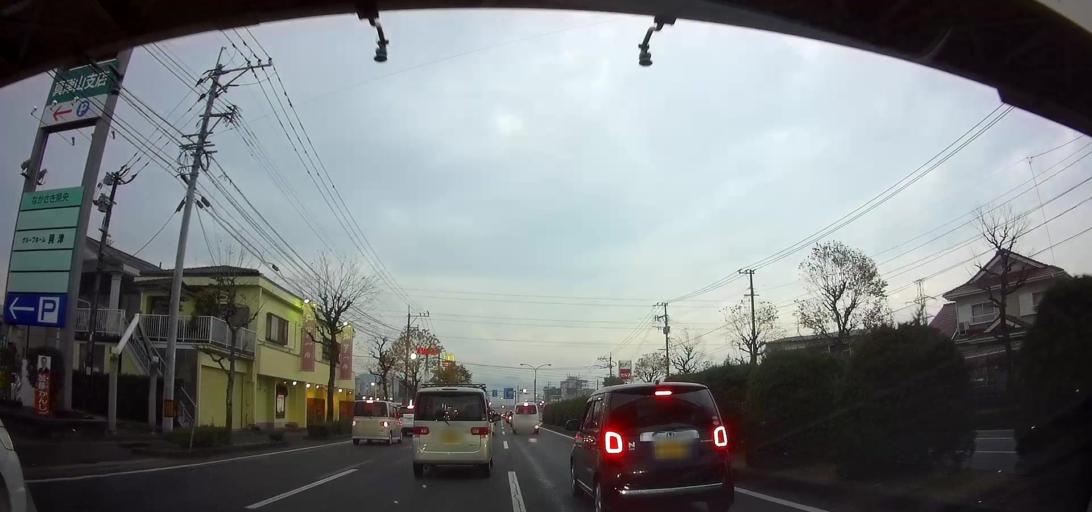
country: JP
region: Nagasaki
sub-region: Isahaya-shi
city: Isahaya
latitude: 32.8374
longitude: 130.0170
